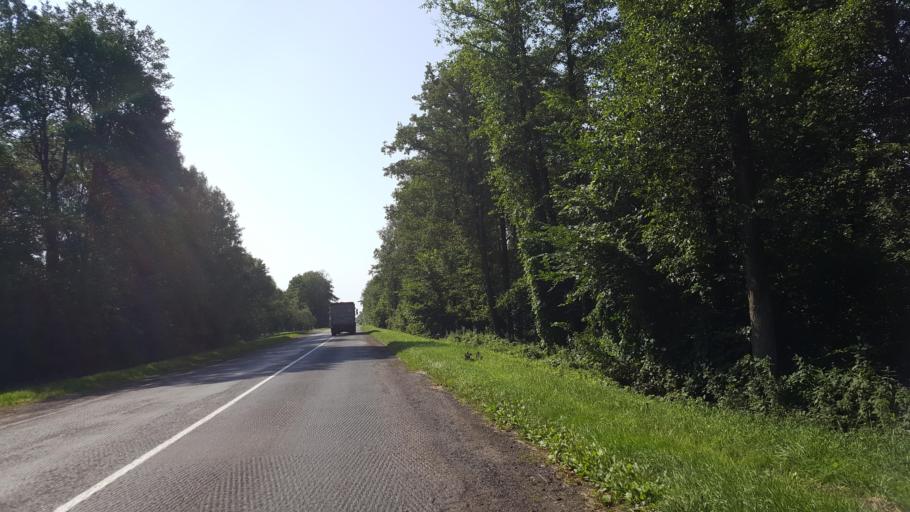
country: BY
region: Brest
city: Zhabinka
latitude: 52.2671
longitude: 23.9581
